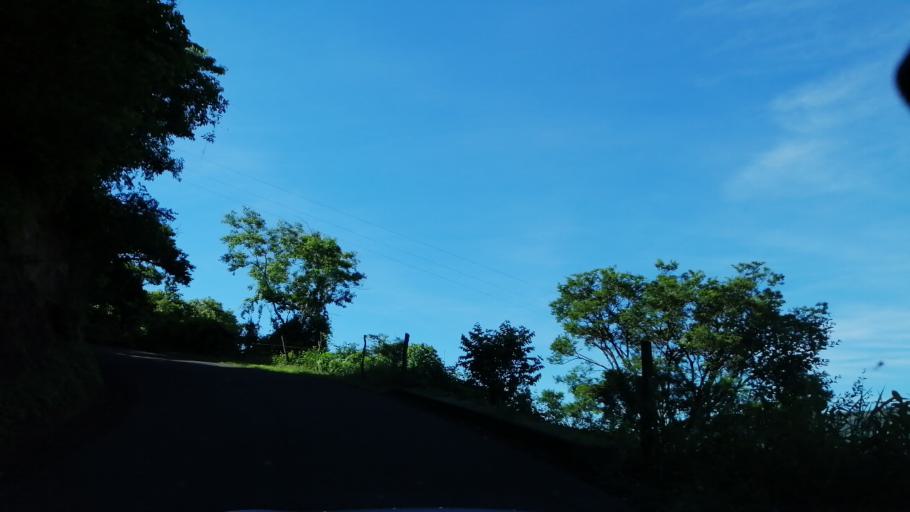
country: SV
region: Morazan
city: Cacaopera
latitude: 13.7827
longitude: -88.0347
